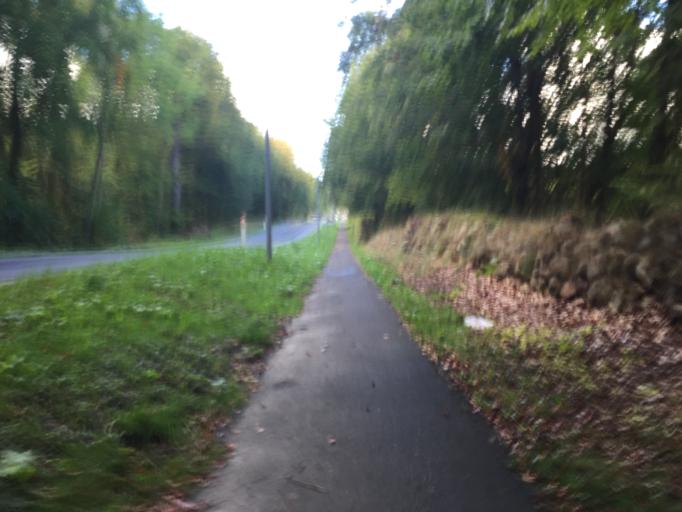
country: DK
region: Capital Region
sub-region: Fureso Kommune
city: Vaerlose
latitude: 55.7712
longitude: 12.3894
